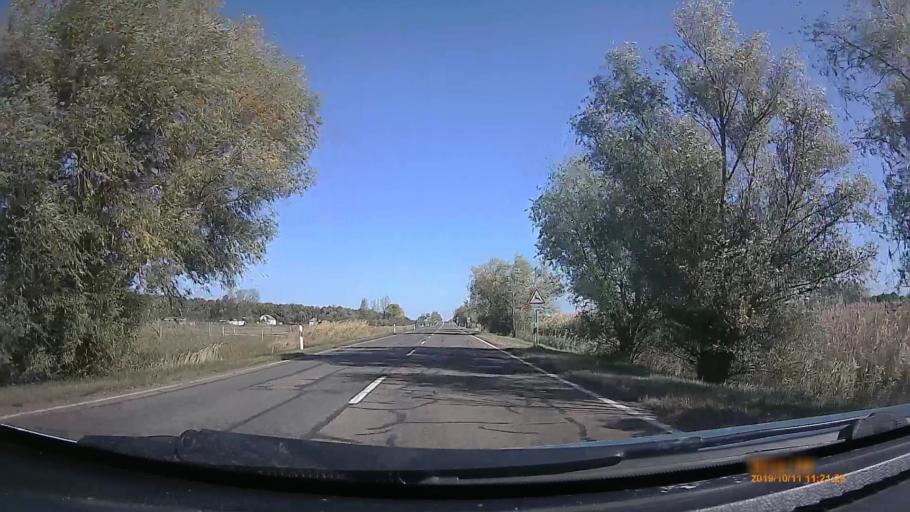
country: HU
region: Hajdu-Bihar
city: Egyek
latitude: 47.5767
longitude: 20.9961
